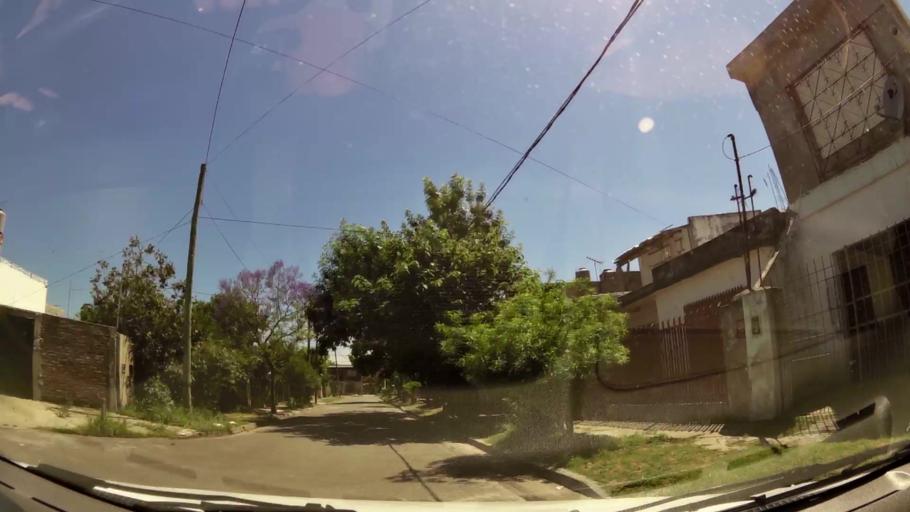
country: AR
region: Buenos Aires
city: Ituzaingo
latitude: -34.6858
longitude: -58.6602
